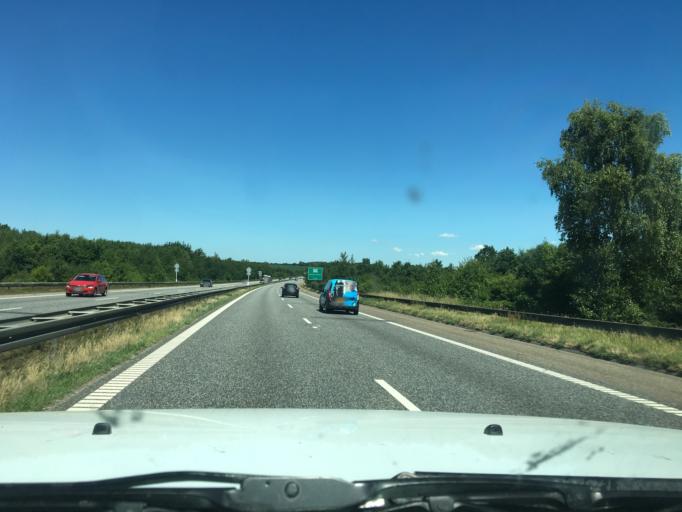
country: DK
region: Central Jutland
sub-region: Arhus Kommune
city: Framlev
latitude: 56.1294
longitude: 10.0346
